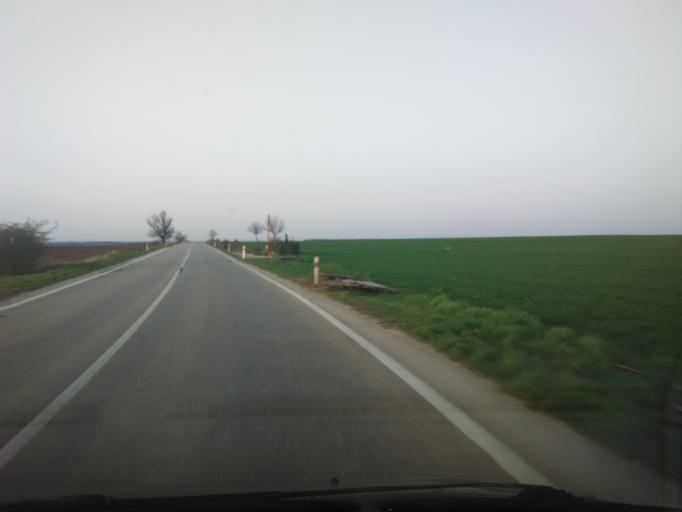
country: SK
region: Nitriansky
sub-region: Okres Nitra
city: Nitra
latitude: 48.2348
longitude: 18.0059
